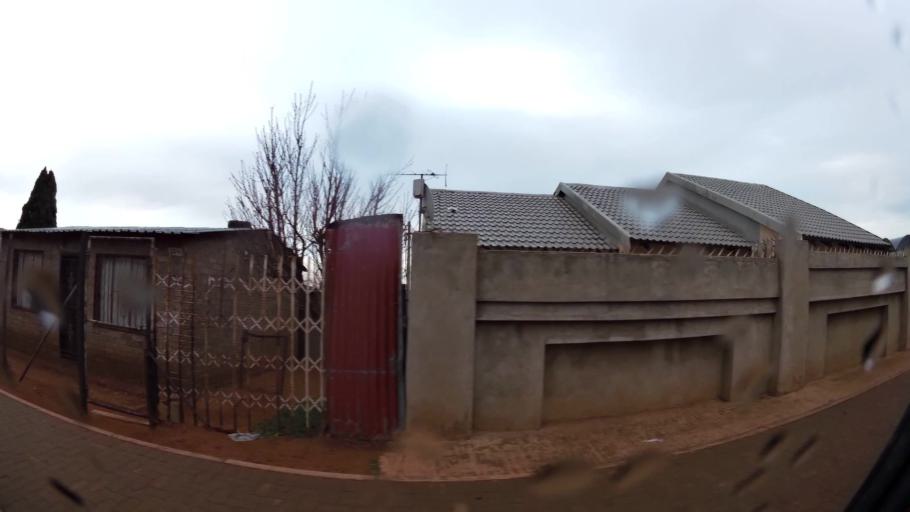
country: ZA
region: Gauteng
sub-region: City of Johannesburg Metropolitan Municipality
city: Roodepoort
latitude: -26.1736
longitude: 27.7877
